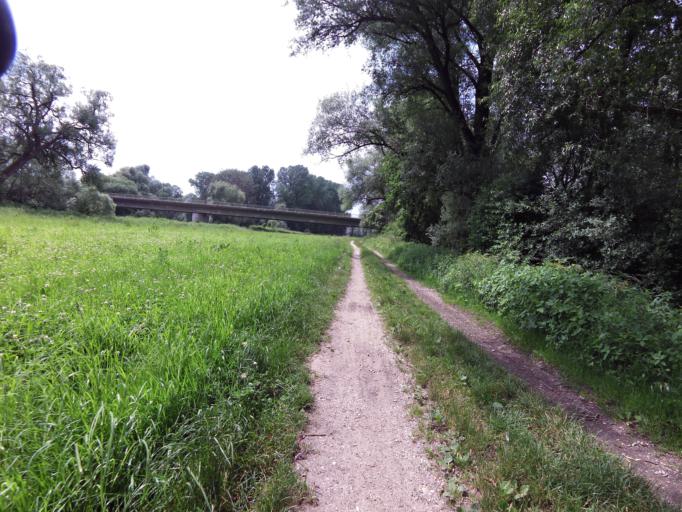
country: DE
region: Bavaria
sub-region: Upper Bavaria
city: Langenbach
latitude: 48.4569
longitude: 11.8537
